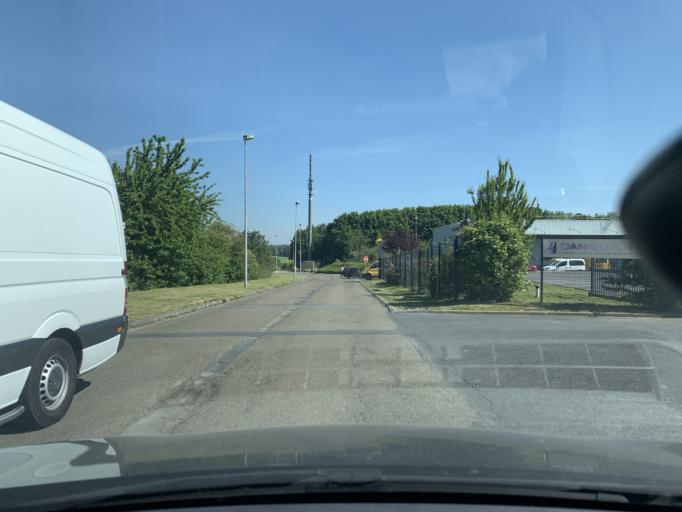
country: FR
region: Nord-Pas-de-Calais
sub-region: Departement du Nord
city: Rumilly-en-Cambresis
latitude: 50.1473
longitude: 3.2245
